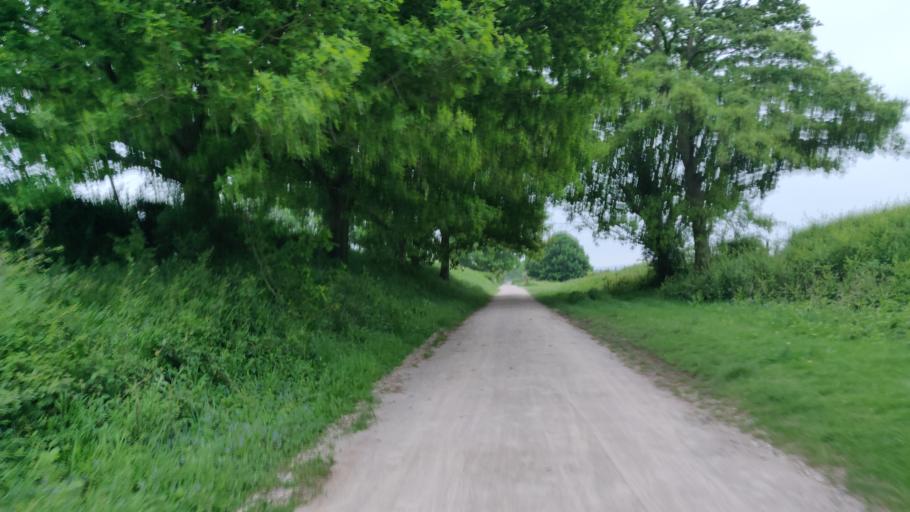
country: GB
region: England
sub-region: West Sussex
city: Partridge Green
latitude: 50.9826
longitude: -0.3152
